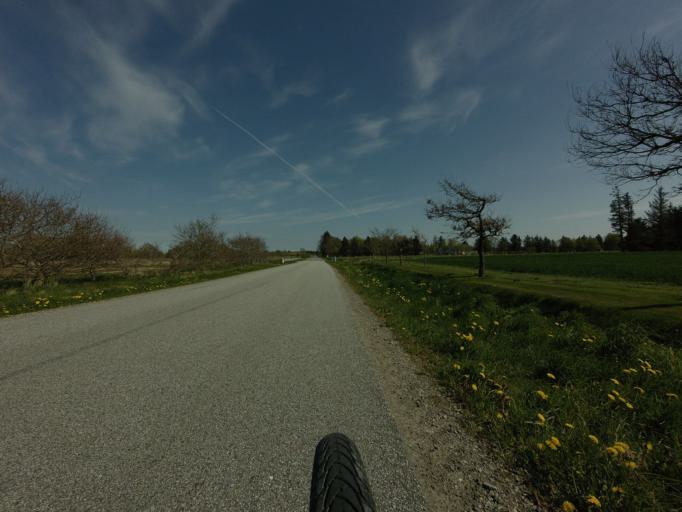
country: DK
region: North Denmark
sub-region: Jammerbugt Kommune
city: Pandrup
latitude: 57.2271
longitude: 9.6327
